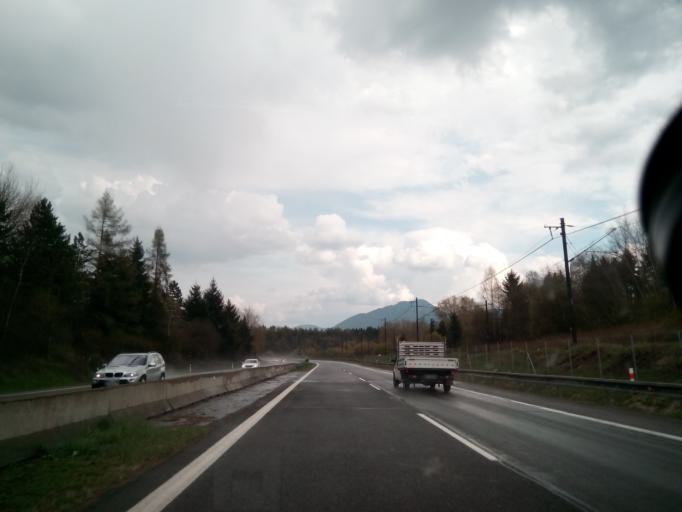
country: SK
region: Zilinsky
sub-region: Okres Liptovsky Mikulas
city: Liptovsky Mikulas
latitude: 49.0893
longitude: 19.5323
